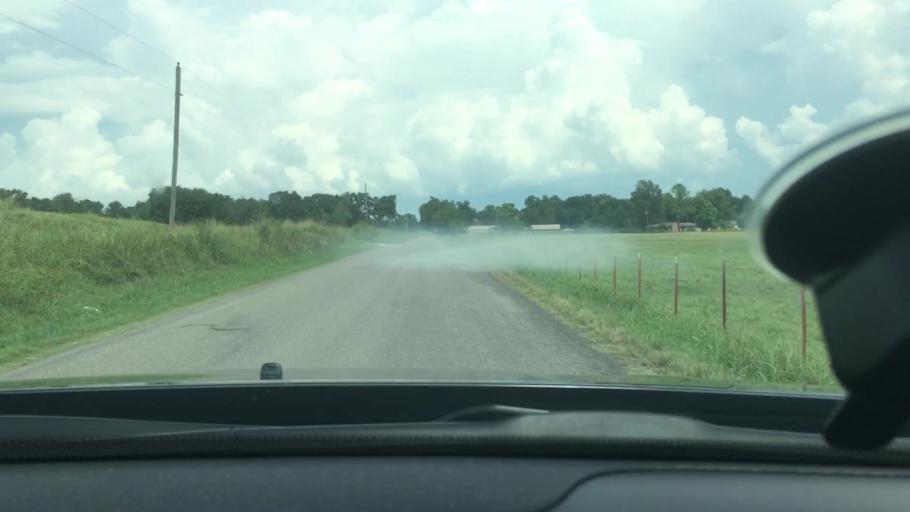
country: US
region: Oklahoma
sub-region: Carter County
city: Dickson
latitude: 34.1985
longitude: -96.8982
